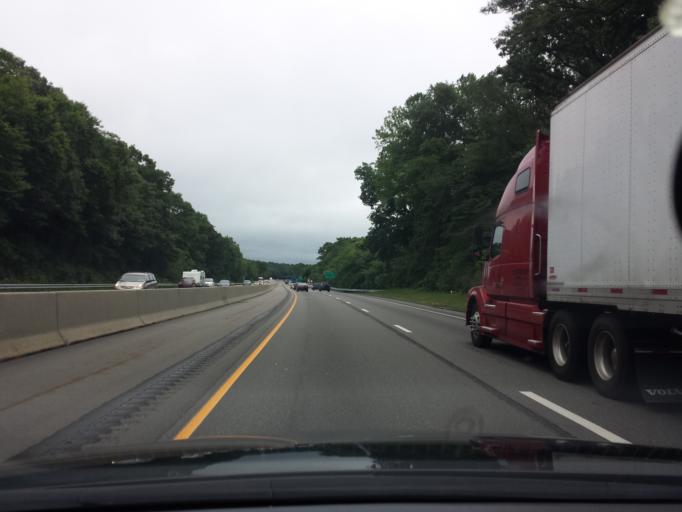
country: US
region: Connecticut
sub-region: Middlesex County
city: Westbrook Center
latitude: 41.2909
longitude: -72.4631
